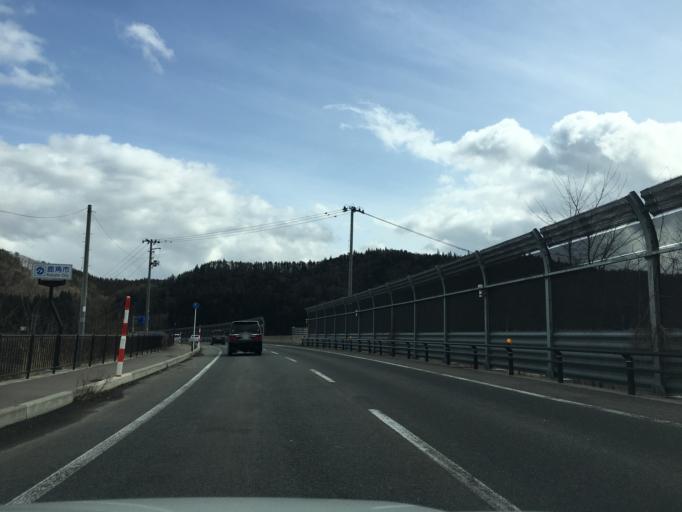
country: JP
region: Akita
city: Hanawa
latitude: 40.2245
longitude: 140.7165
